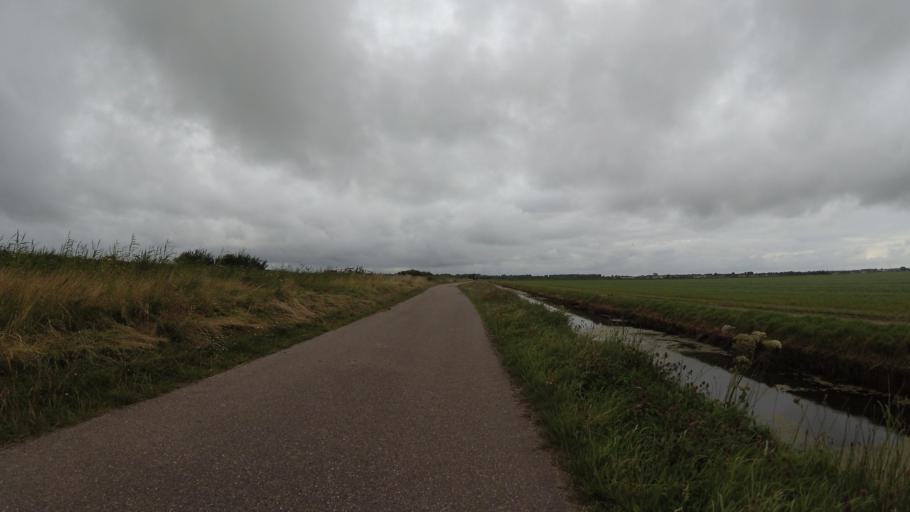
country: NL
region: North Holland
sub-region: Gemeente Den Helder
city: Den Helder
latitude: 52.9164
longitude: 4.7285
